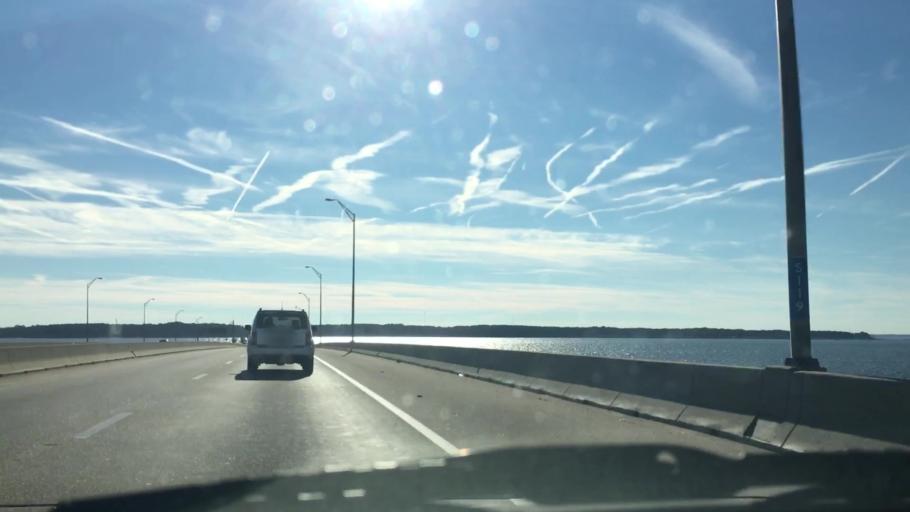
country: US
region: Virginia
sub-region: City of Newport News
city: Newport News
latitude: 36.9198
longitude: -76.4134
